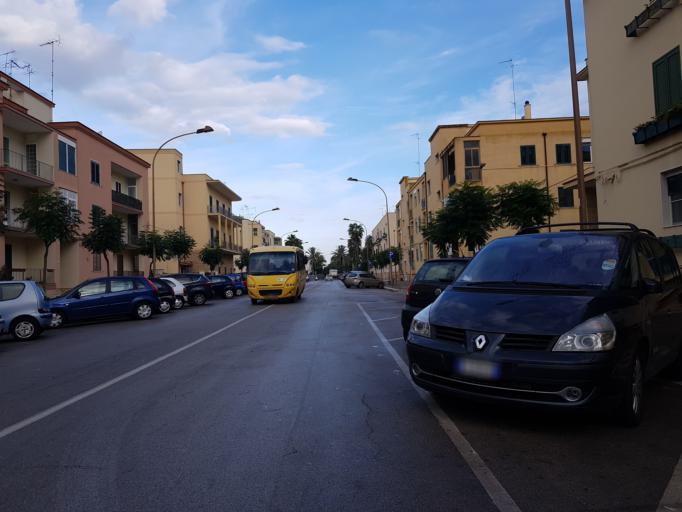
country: IT
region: Apulia
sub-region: Provincia di Brindisi
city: Materdomini
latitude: 40.6459
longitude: 17.9463
